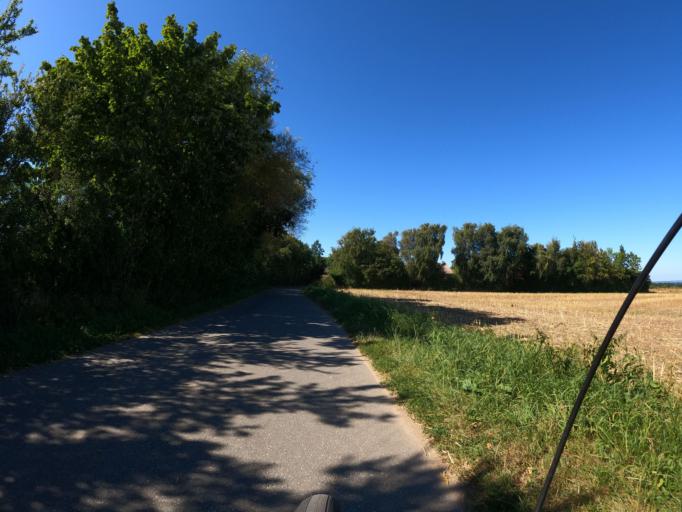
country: DE
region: Schleswig-Holstein
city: Steinberg
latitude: 54.7825
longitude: 9.7607
